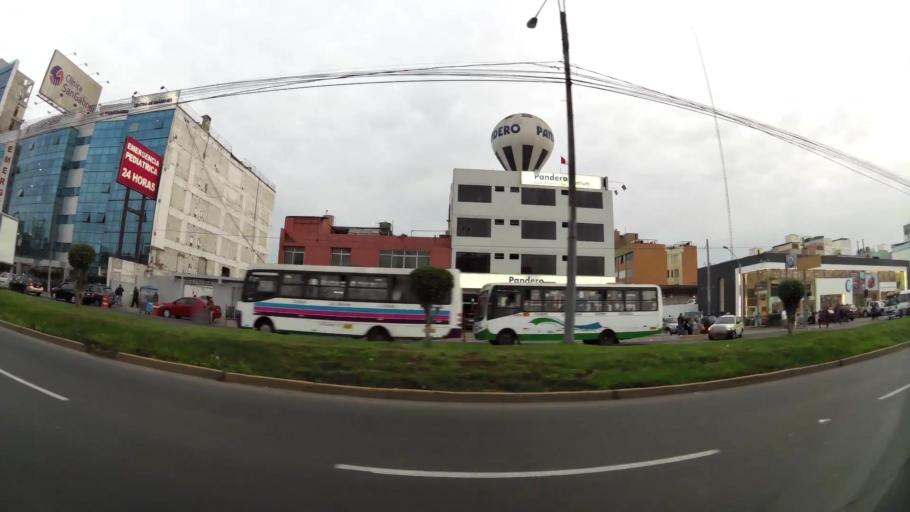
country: PE
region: Callao
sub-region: Callao
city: Callao
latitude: -12.0762
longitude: -77.0960
